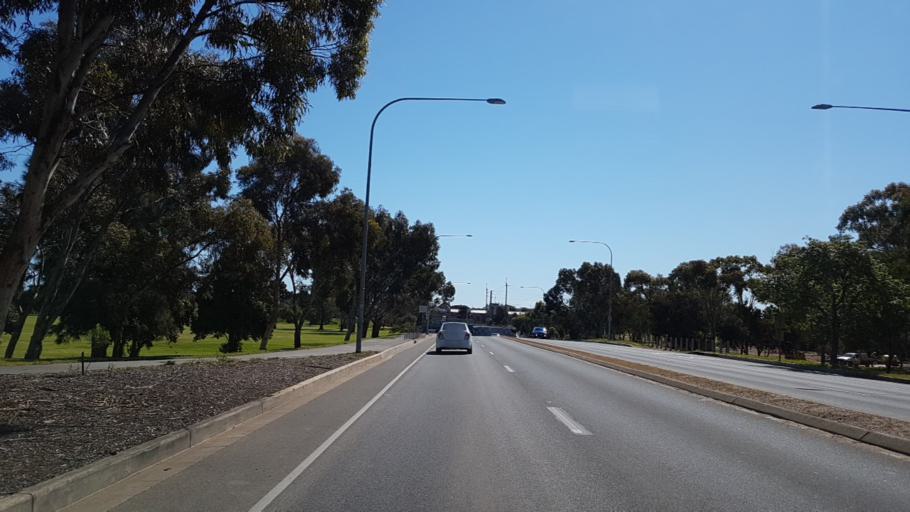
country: AU
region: South Australia
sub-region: Adelaide
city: Adelaide
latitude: -34.9243
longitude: 138.5839
